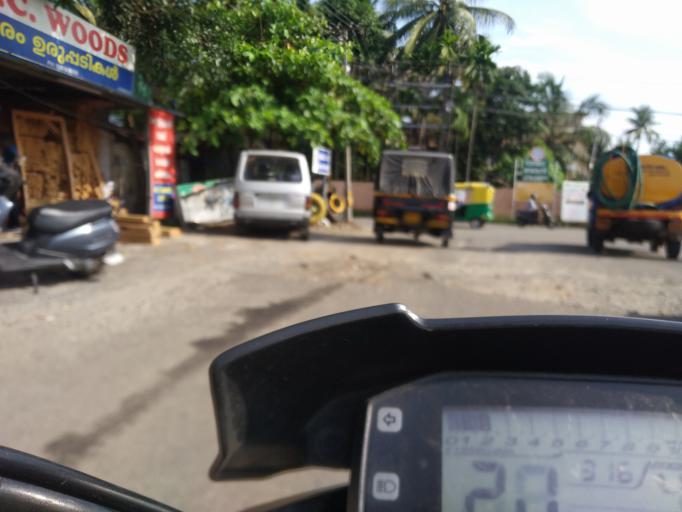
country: IN
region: Kerala
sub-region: Ernakulam
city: Cochin
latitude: 9.9843
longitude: 76.3041
